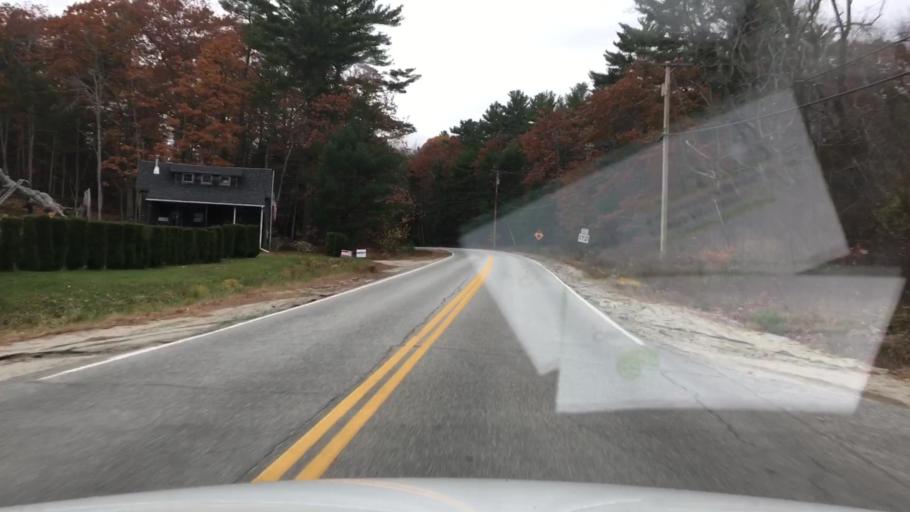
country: US
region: Maine
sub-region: Hancock County
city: Sedgwick
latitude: 44.3792
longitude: -68.5664
